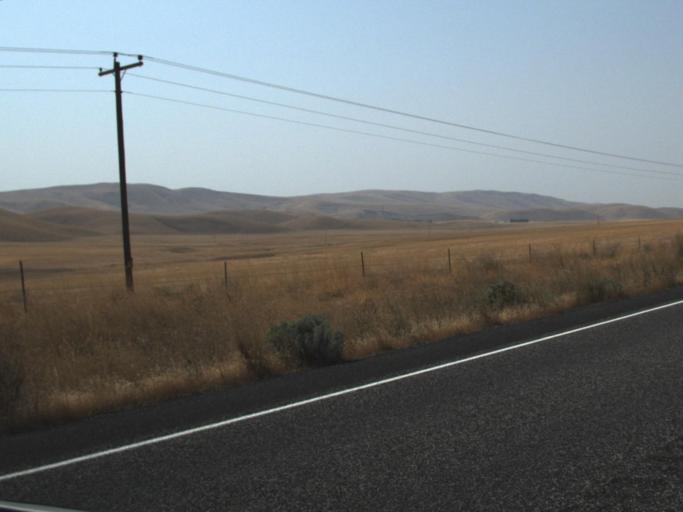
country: US
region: Washington
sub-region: Grant County
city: Desert Aire
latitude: 46.5197
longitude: -119.9889
